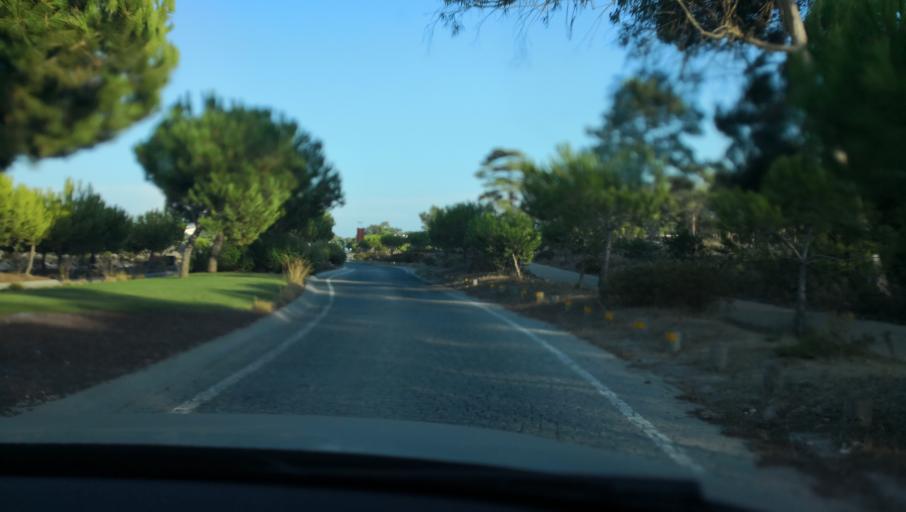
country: PT
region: Setubal
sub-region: Setubal
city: Setubal
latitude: 38.4651
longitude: -8.8710
